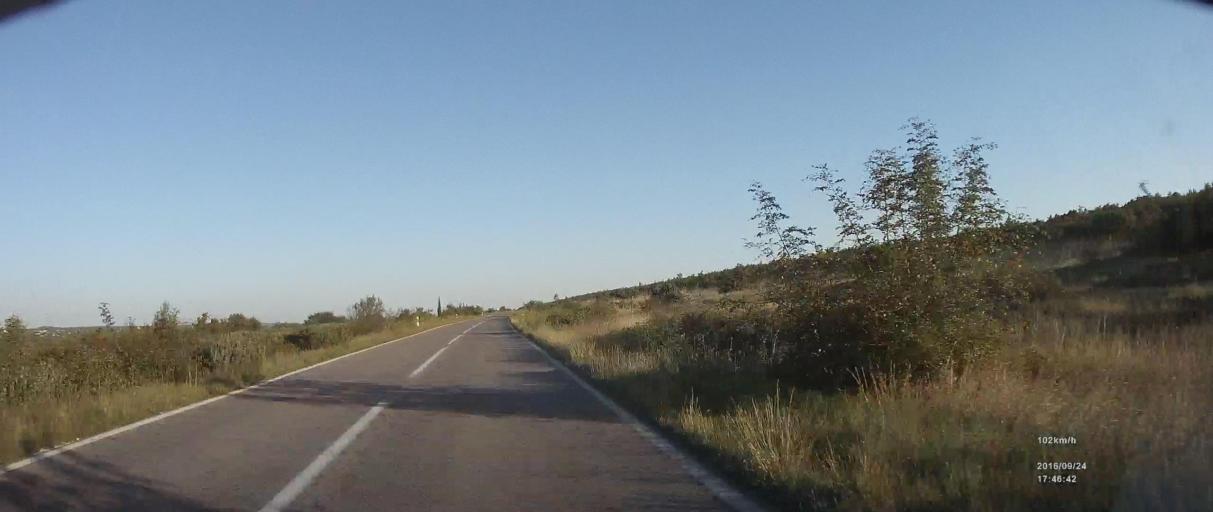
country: HR
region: Zadarska
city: Polaca
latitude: 44.0845
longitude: 15.5116
